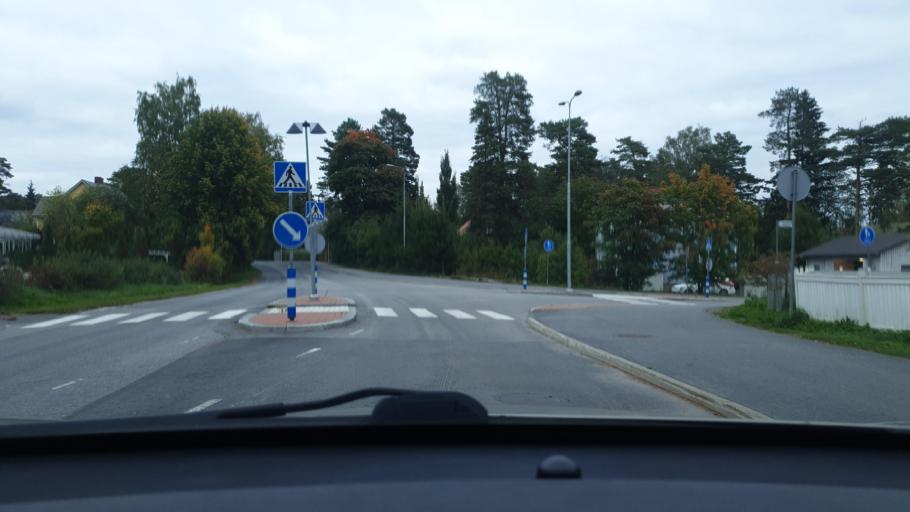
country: FI
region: Ostrobothnia
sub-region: Vaasa
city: Korsholm
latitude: 63.1001
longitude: 21.6714
